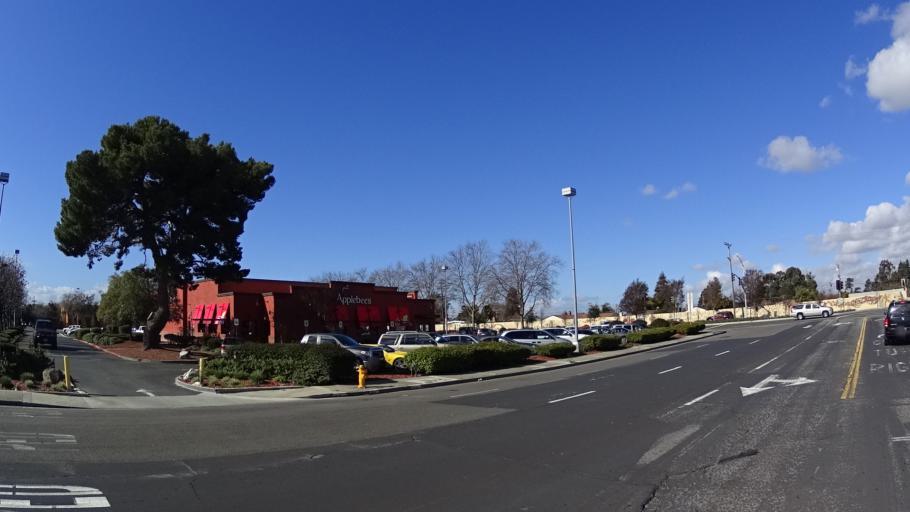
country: US
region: California
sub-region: Alameda County
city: Cherryland
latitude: 37.6543
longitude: -122.1051
